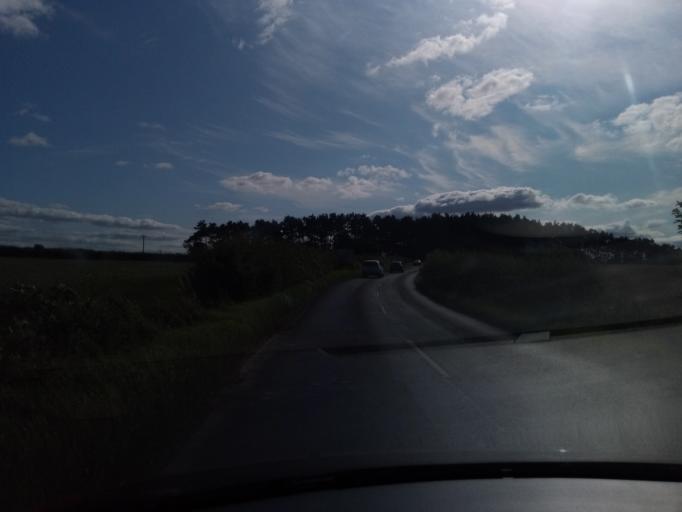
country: GB
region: Scotland
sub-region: The Scottish Borders
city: Allanton
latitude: 55.7569
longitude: -2.1280
